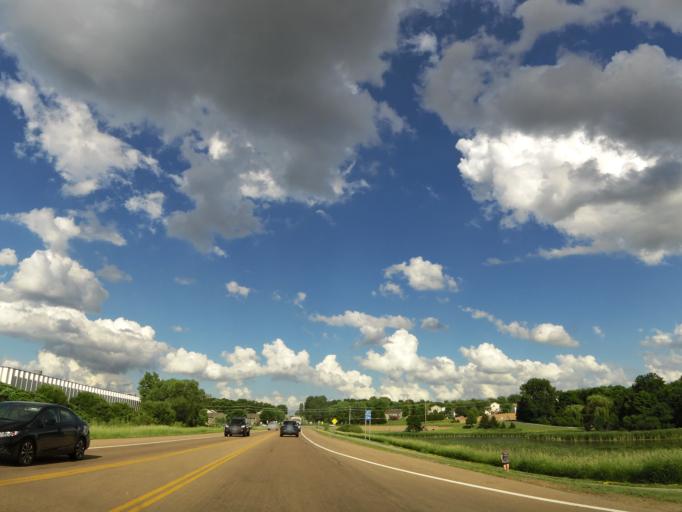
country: US
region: Minnesota
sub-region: Carver County
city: Waconia
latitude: 44.8365
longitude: -93.7927
